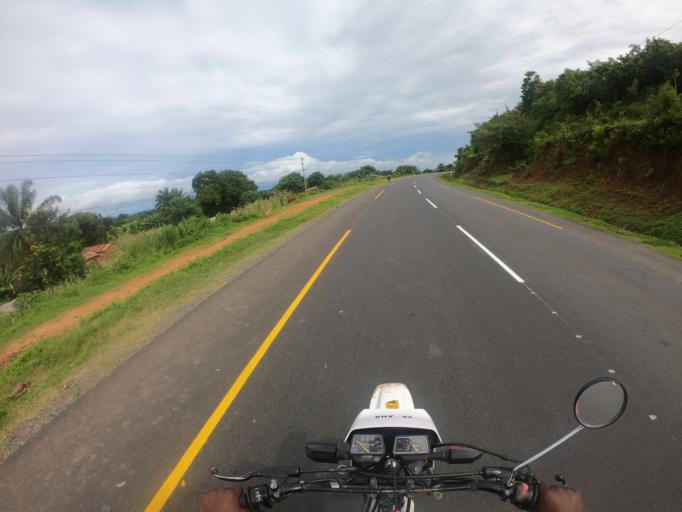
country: TZ
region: Mbeya
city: Kyela
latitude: -9.7051
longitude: 33.8655
